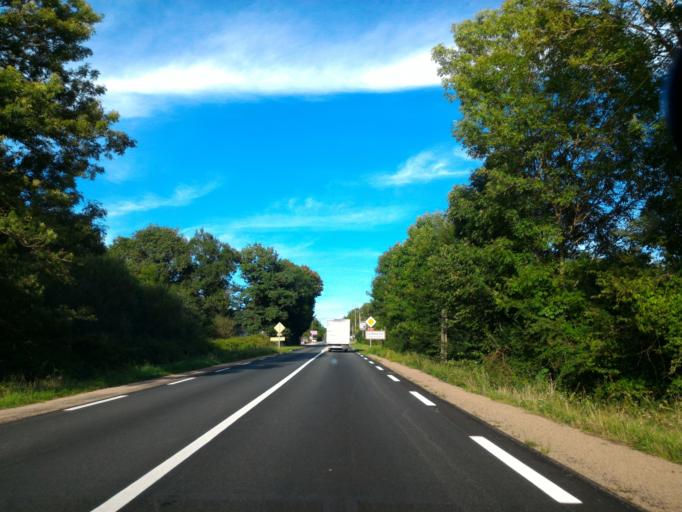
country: FR
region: Limousin
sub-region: Departement de la Haute-Vienne
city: Magnac-Laval
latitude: 46.1653
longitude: 1.1396
